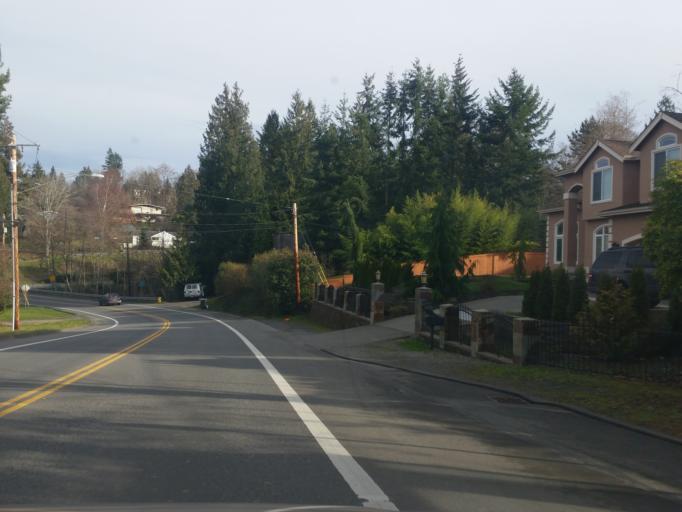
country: US
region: Washington
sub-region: Snohomish County
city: Mukilteo
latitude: 47.9535
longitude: -122.2637
